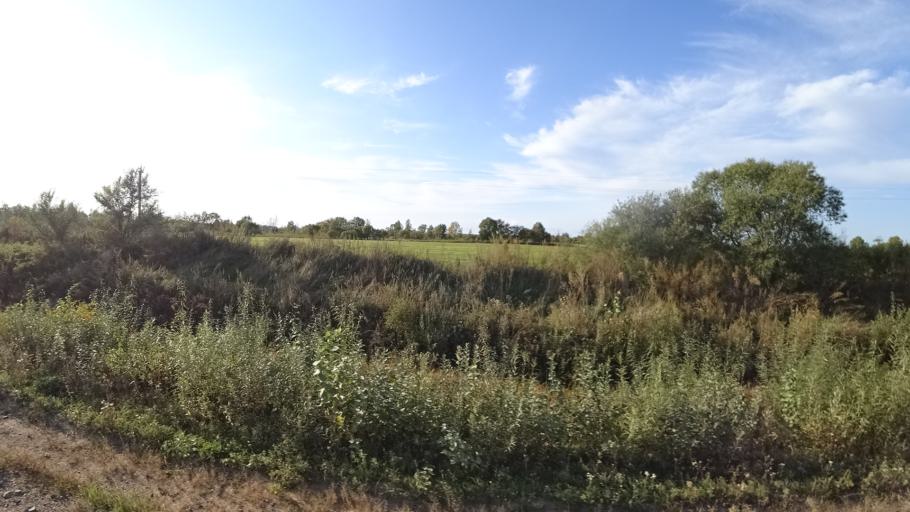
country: RU
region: Amur
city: Arkhara
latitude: 49.3526
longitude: 130.1341
